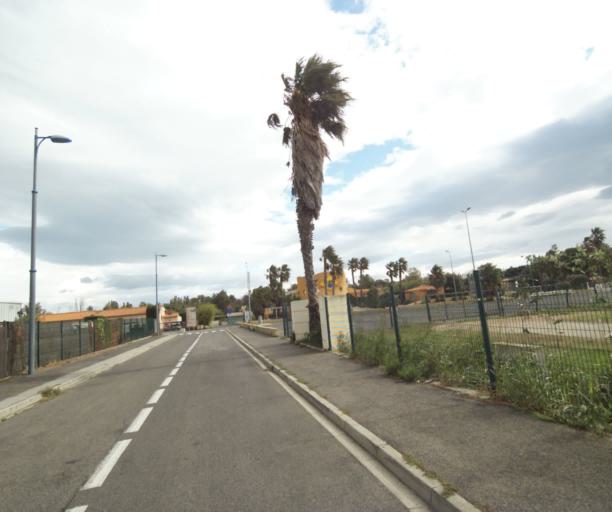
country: FR
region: Languedoc-Roussillon
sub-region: Departement des Pyrenees-Orientales
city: Argelers
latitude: 42.5763
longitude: 3.0354
